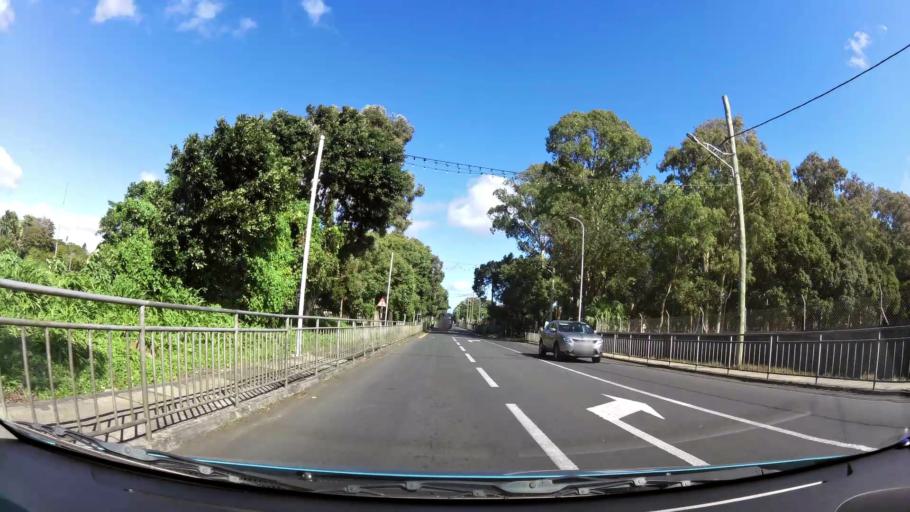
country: MU
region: Plaines Wilhems
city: Vacoas
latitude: -20.2962
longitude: 57.4983
